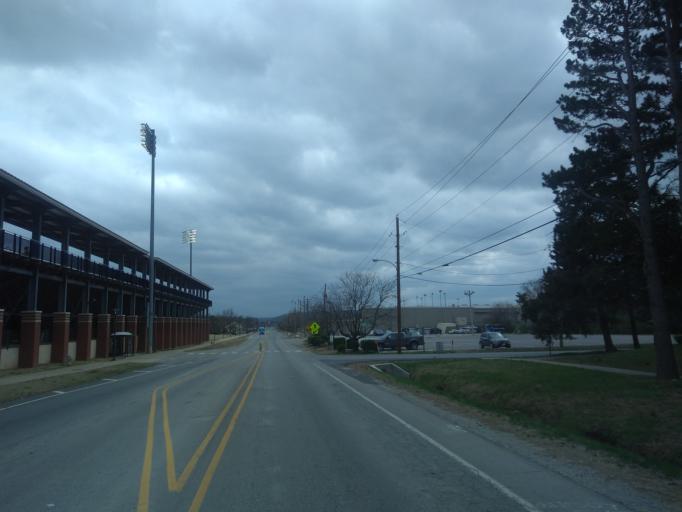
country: US
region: Arkansas
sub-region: Washington County
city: Fayetteville
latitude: 36.0636
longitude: -94.1802
